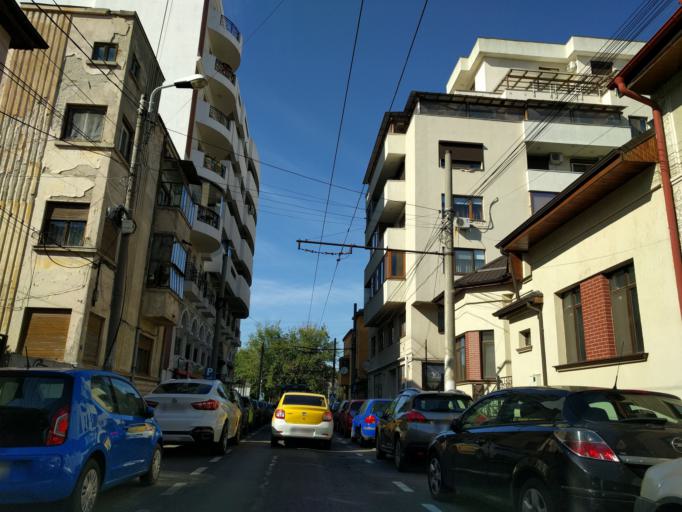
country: RO
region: Bucuresti
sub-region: Municipiul Bucuresti
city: Bucharest
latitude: 44.4348
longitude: 26.1265
